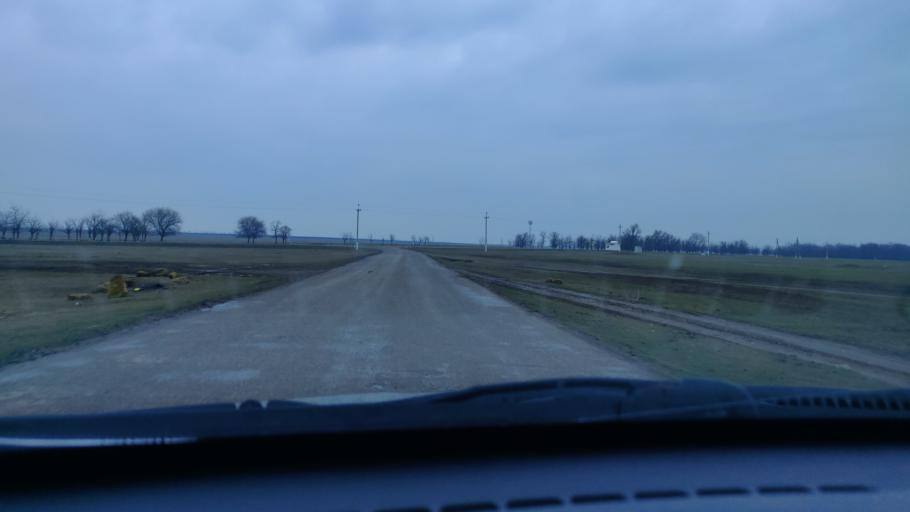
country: RU
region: Stavropol'skiy
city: Letnyaya Stavka
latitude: 45.4122
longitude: 43.7051
